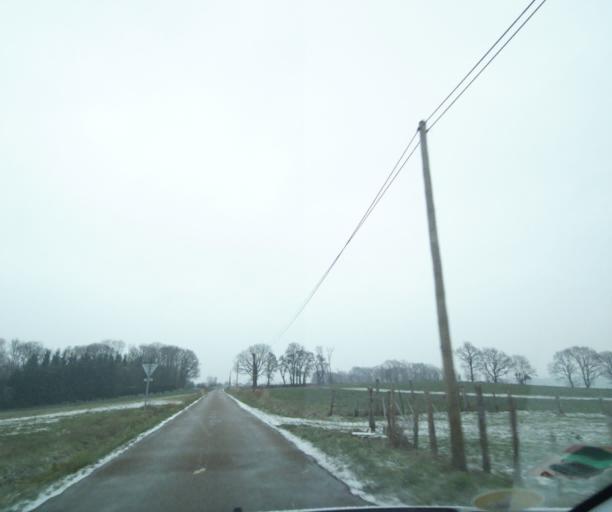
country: FR
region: Champagne-Ardenne
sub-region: Departement de la Haute-Marne
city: Wassy
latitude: 48.4635
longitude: 5.0343
